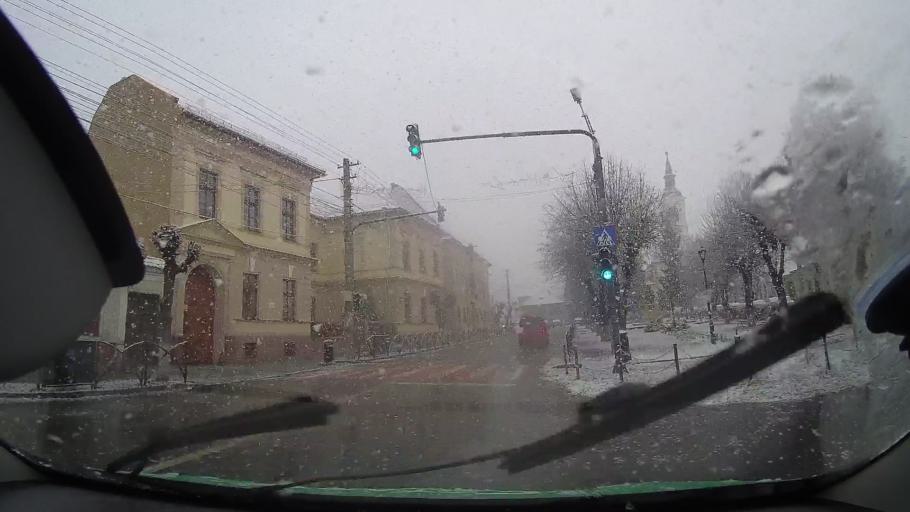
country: RO
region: Sibiu
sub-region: Municipiul Medias
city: Medias
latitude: 46.1671
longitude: 24.3536
